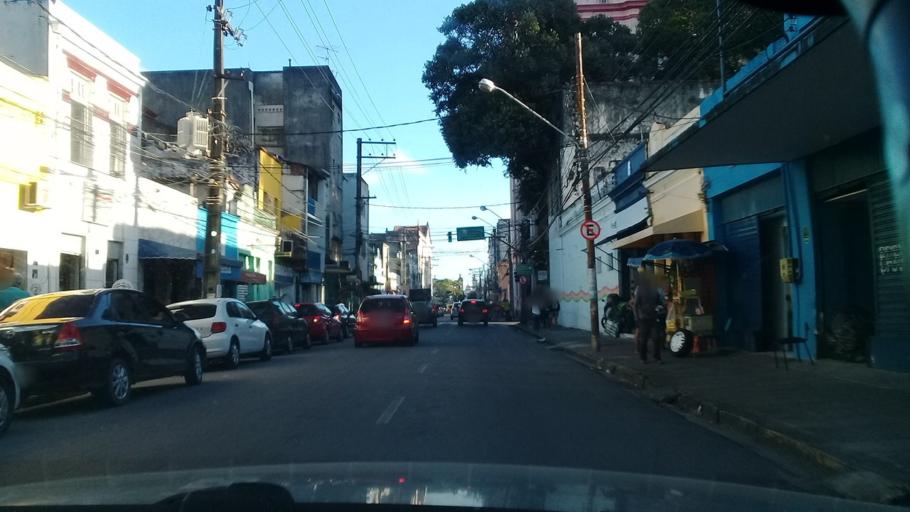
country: BR
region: Pernambuco
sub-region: Recife
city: Recife
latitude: -8.0606
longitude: -34.8871
